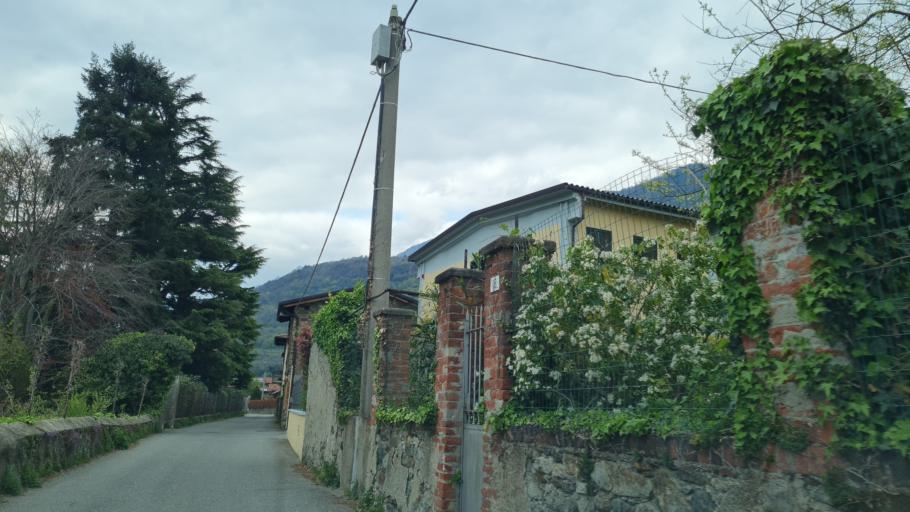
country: IT
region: Piedmont
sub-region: Provincia di Torino
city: Borgofranco d'Ivrea
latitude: 45.5265
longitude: 7.8517
